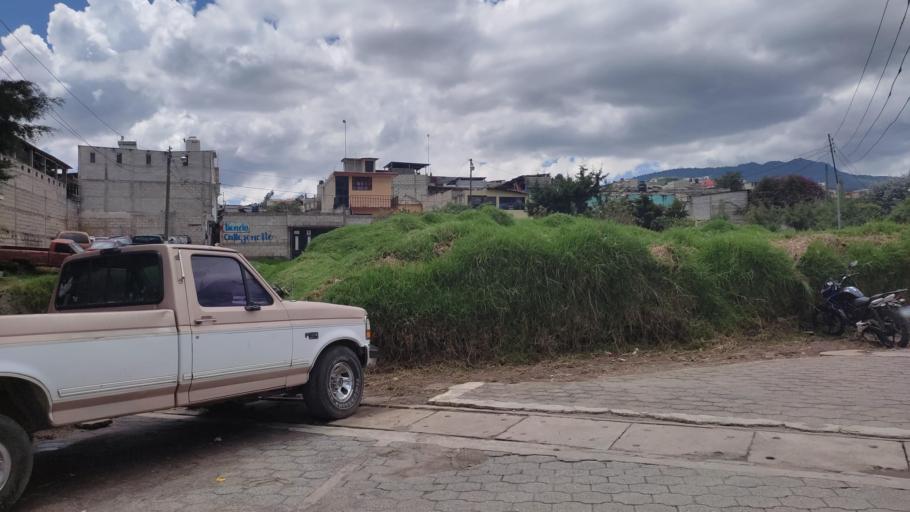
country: GT
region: Quetzaltenango
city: Quetzaltenango
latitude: 14.8554
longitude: -91.5255
